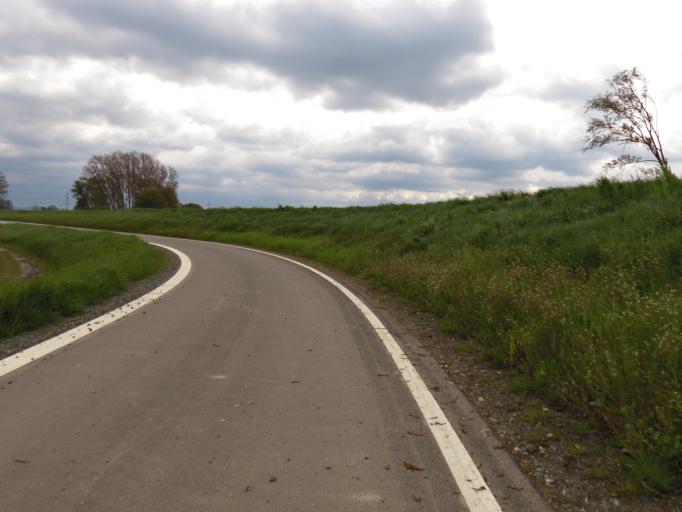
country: DE
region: Rheinland-Pfalz
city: Eich
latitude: 49.6987
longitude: 8.4015
